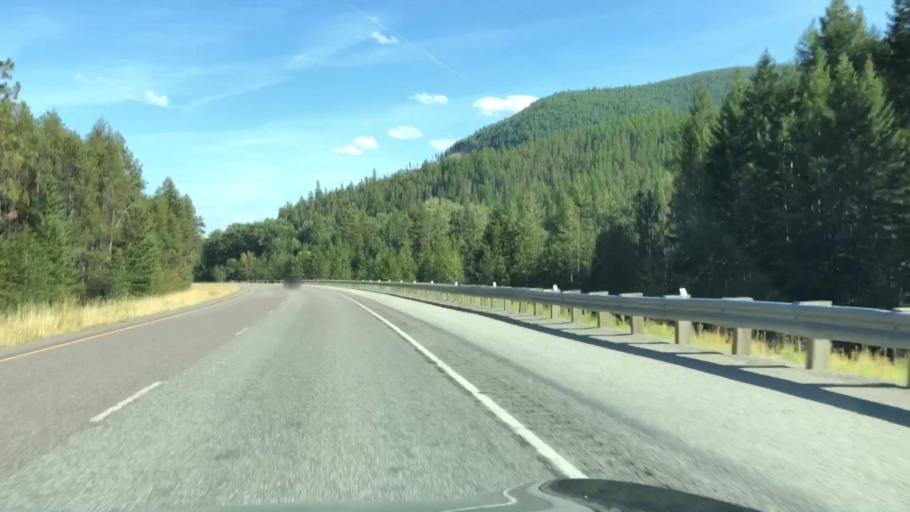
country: US
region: Montana
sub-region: Sanders County
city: Thompson Falls
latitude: 47.4056
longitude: -115.4887
